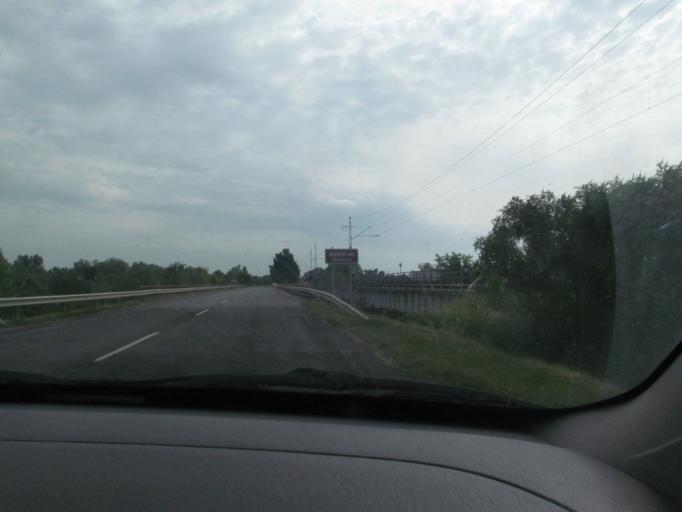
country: HU
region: Szabolcs-Szatmar-Bereg
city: Rakamaz
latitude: 48.1250
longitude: 21.4464
